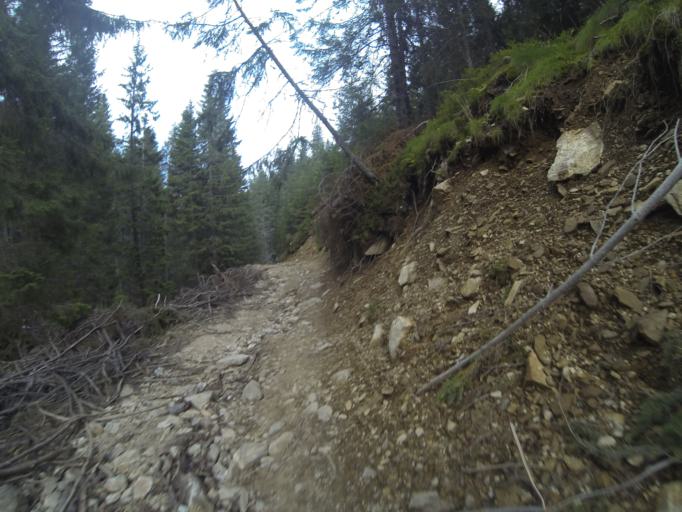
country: RO
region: Gorj
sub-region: Comuna Polovragi
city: Polovragi
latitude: 45.2979
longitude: 23.8385
